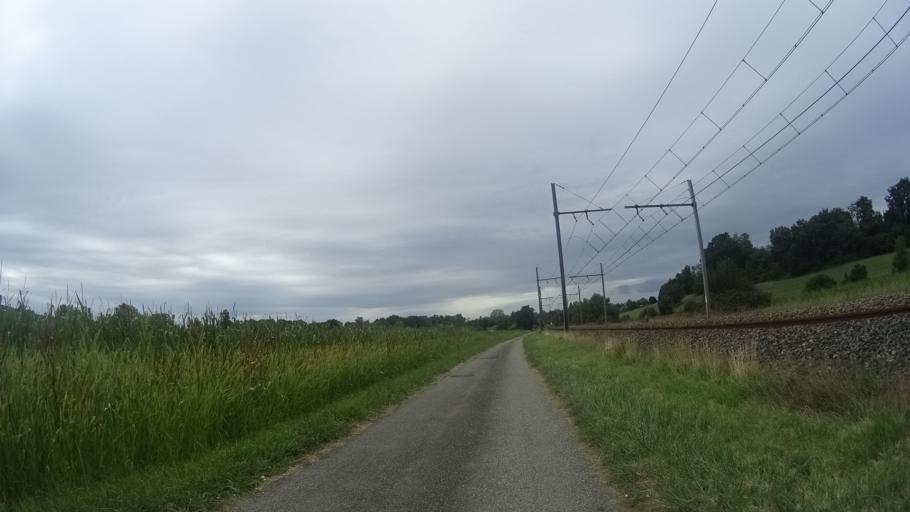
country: FR
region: Aquitaine
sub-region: Departement des Pyrenees-Atlantiques
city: Orthez
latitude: 43.4679
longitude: -0.7220
